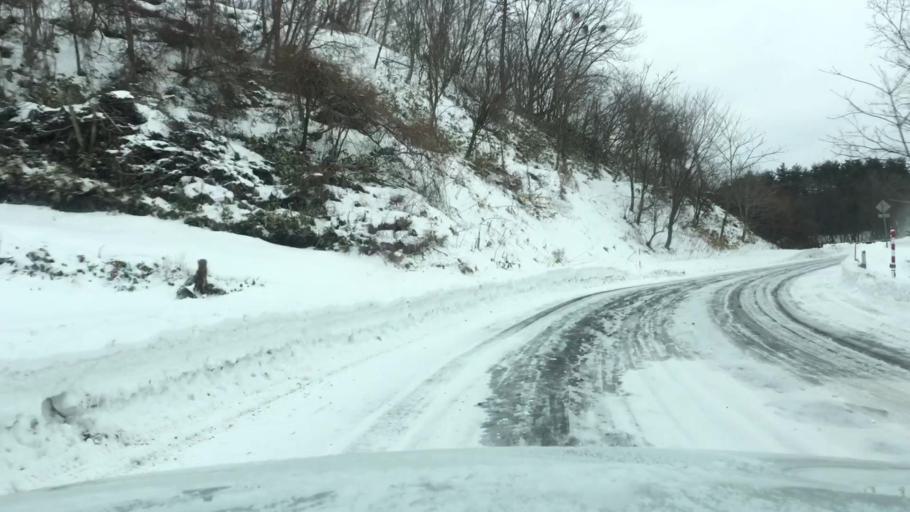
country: JP
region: Iwate
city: Shizukuishi
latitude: 39.9440
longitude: 140.9967
